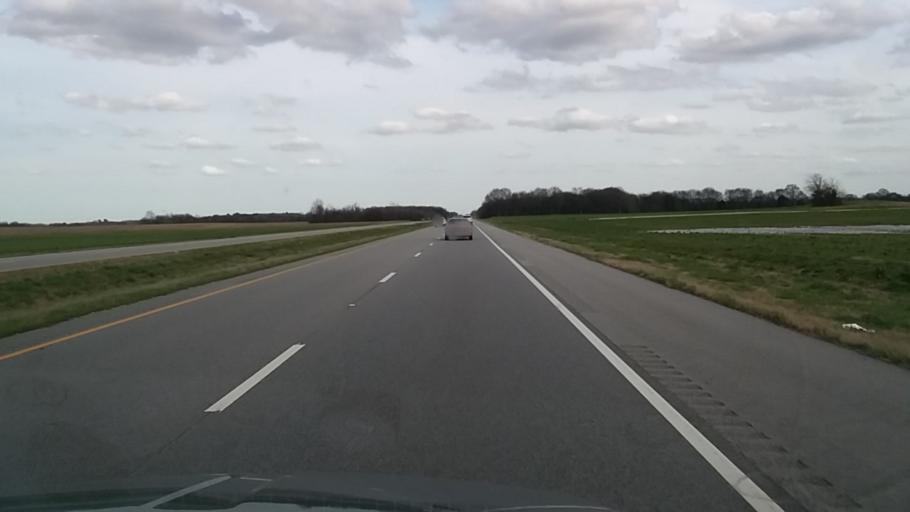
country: US
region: Alabama
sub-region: Lawrence County
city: Town Creek
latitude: 34.6832
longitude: -87.5007
